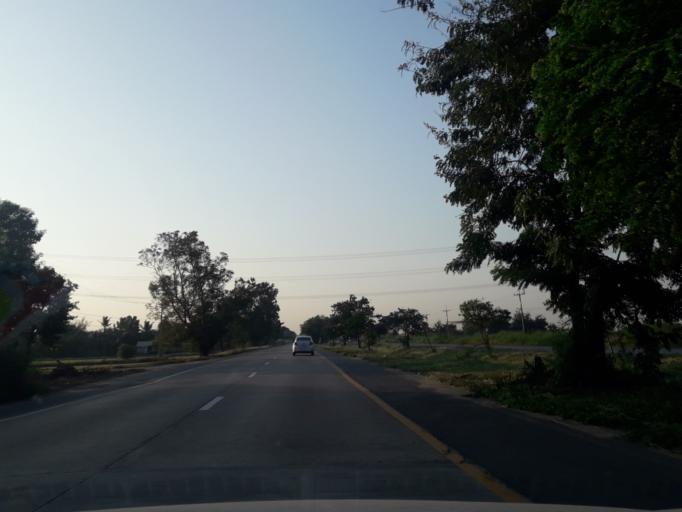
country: TH
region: Phra Nakhon Si Ayutthaya
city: Bang Pa-in
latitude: 14.2734
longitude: 100.5302
